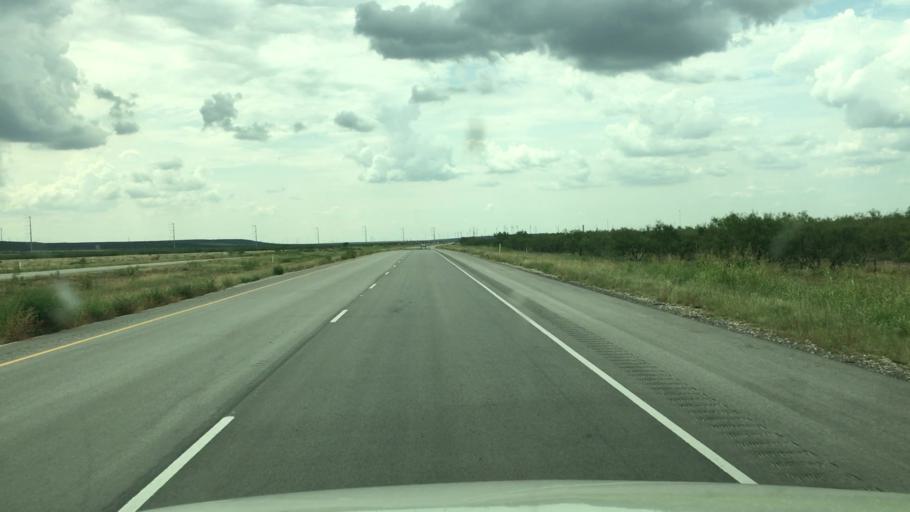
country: US
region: Texas
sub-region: Sterling County
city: Sterling City
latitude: 31.9623
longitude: -101.2175
